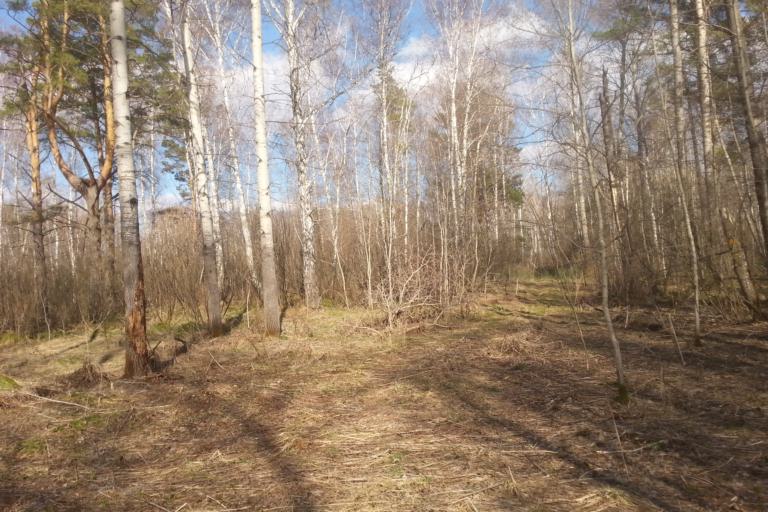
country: RU
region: Altai Krai
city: Sannikovo
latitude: 53.3306
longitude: 84.0251
